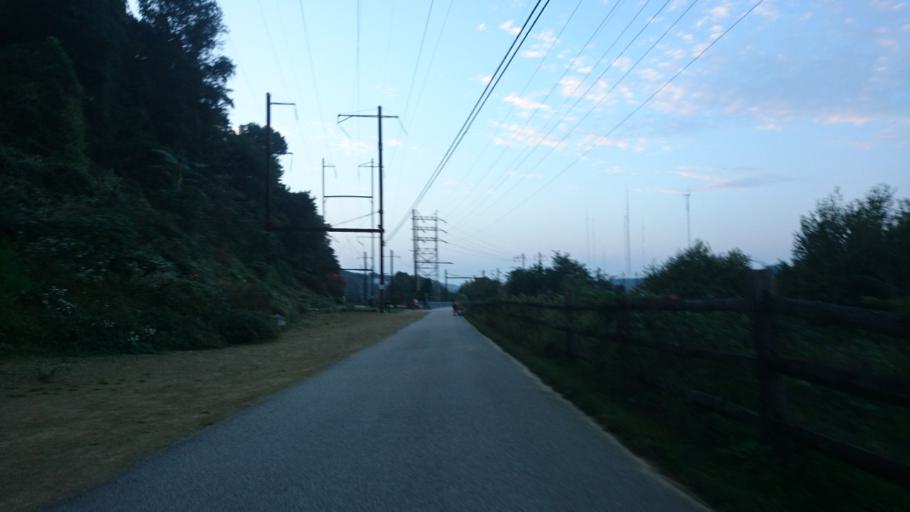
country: US
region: Pennsylvania
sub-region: Montgomery County
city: Bala-Cynwyd
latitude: 40.0224
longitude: -75.2244
